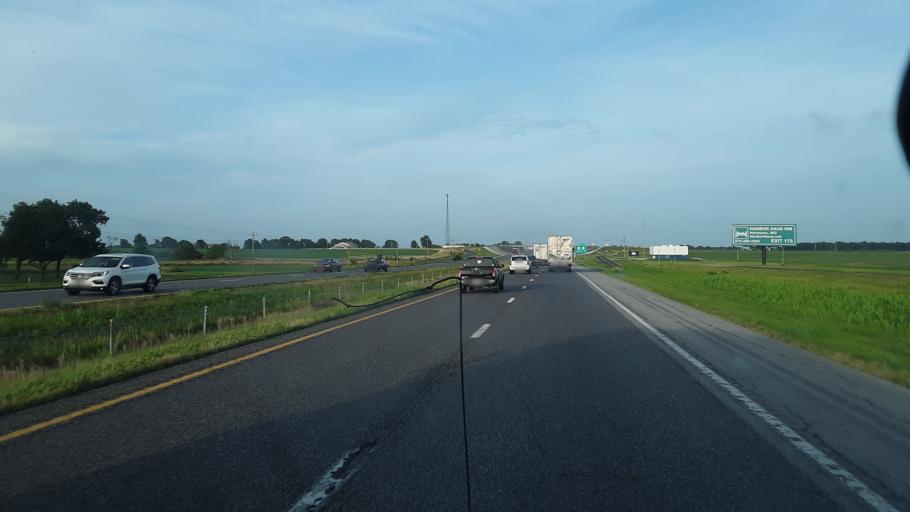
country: US
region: Missouri
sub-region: Callaway County
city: Fulton
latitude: 38.9519
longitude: -92.0170
